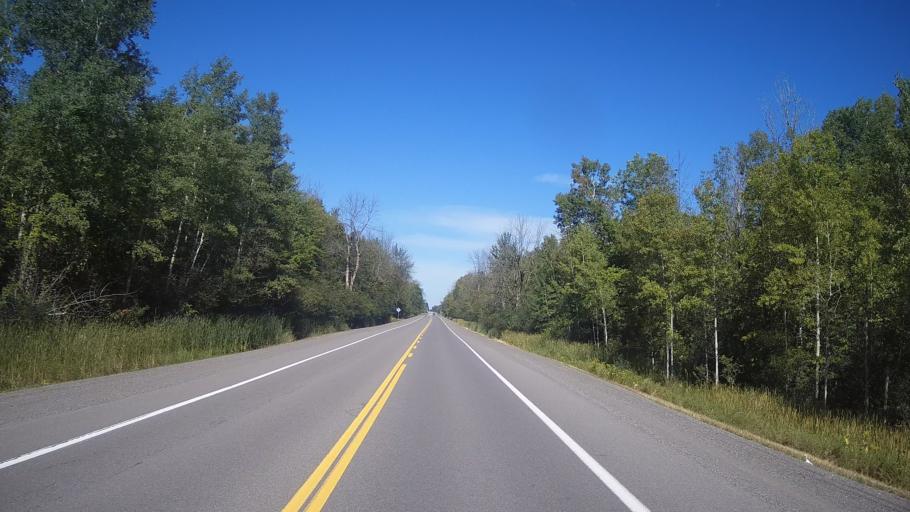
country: CA
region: Ontario
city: Bells Corners
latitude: 45.0783
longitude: -75.6494
